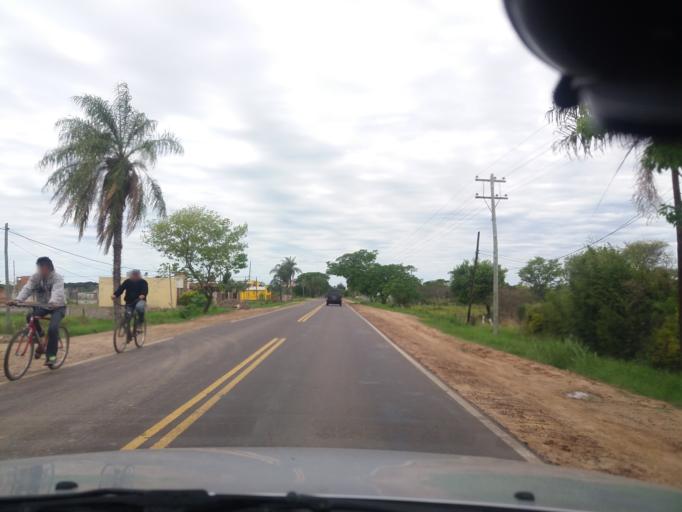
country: AR
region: Corrientes
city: Corrientes
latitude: -27.4492
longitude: -58.7461
